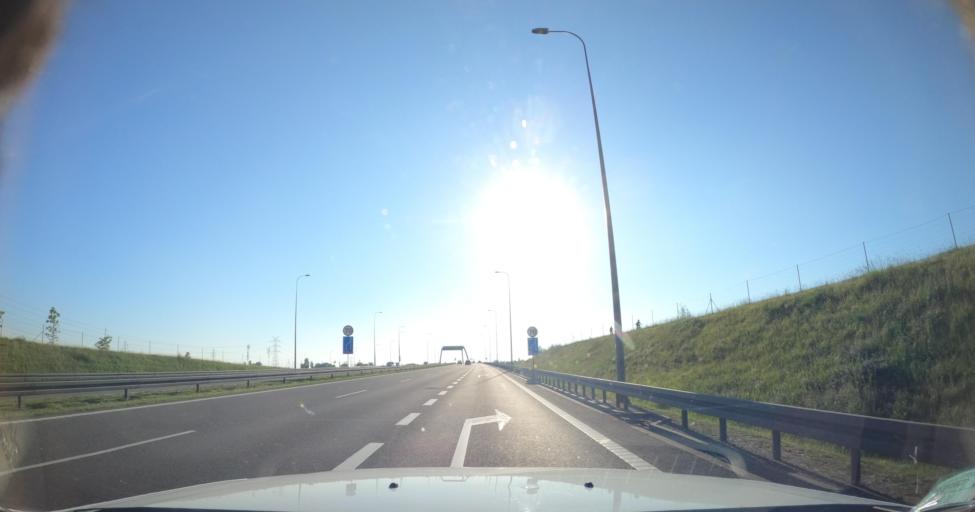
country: PL
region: Pomeranian Voivodeship
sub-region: Powiat gdanski
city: Rotmanka
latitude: 54.2900
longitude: 18.5920
